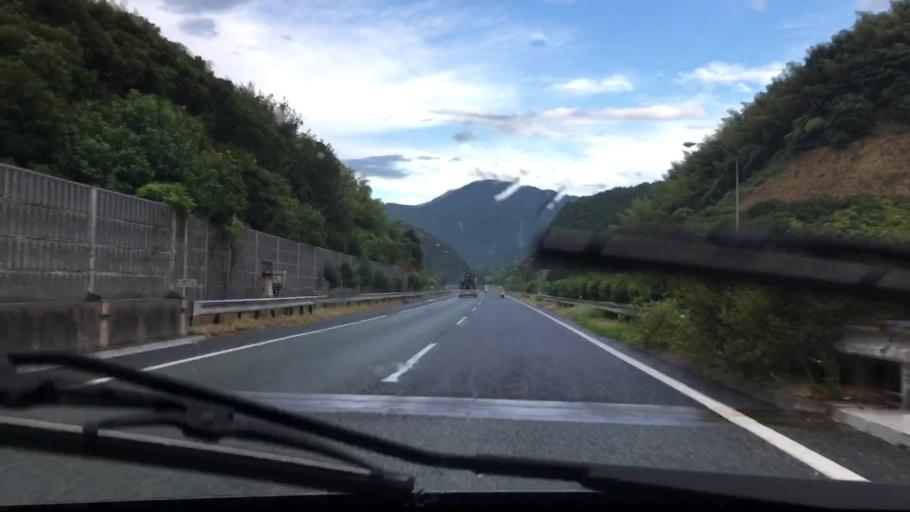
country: JP
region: Fukuoka
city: Kitakyushu
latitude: 33.8038
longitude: 130.8529
